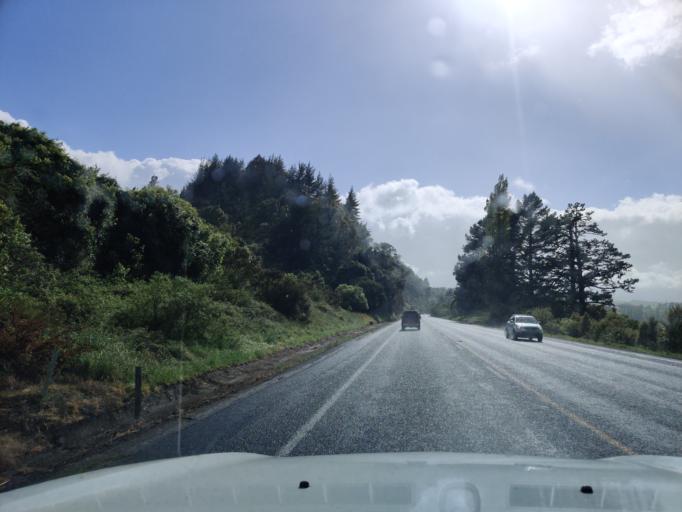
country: NZ
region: Waikato
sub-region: Matamata-Piako District
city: Matamata
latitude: -37.9498
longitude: 175.6365
